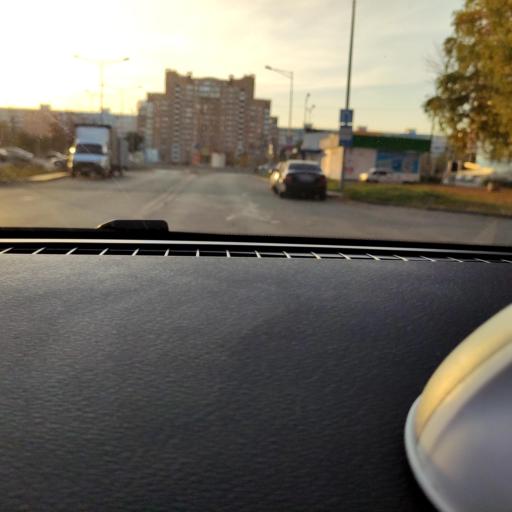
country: RU
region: Samara
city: Samara
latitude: 53.2543
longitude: 50.2254
